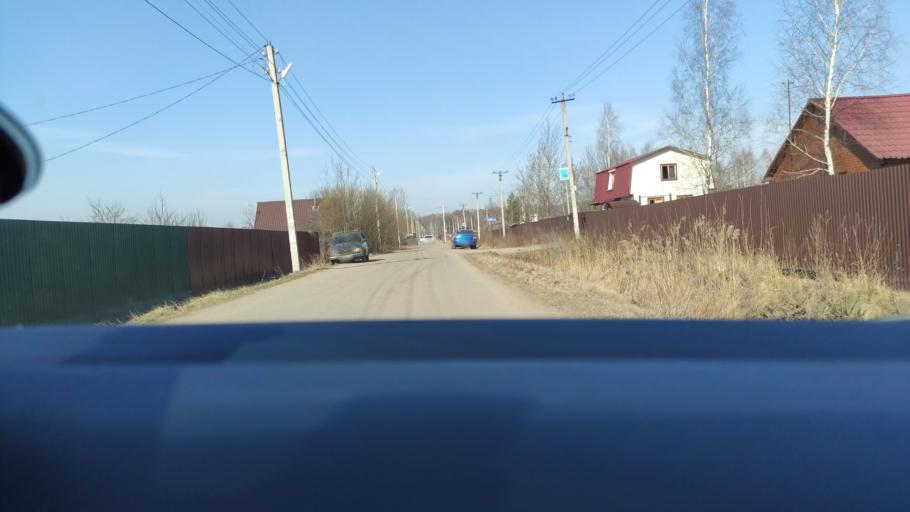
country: RU
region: Moskovskaya
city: Imeni Vorovskogo
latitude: 55.7789
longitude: 38.3692
